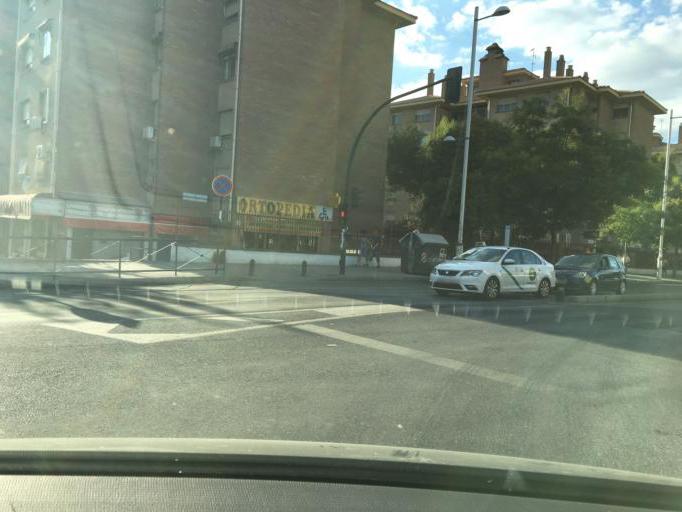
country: ES
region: Andalusia
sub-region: Provincia de Granada
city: Granada
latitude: 37.1918
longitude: -3.6077
